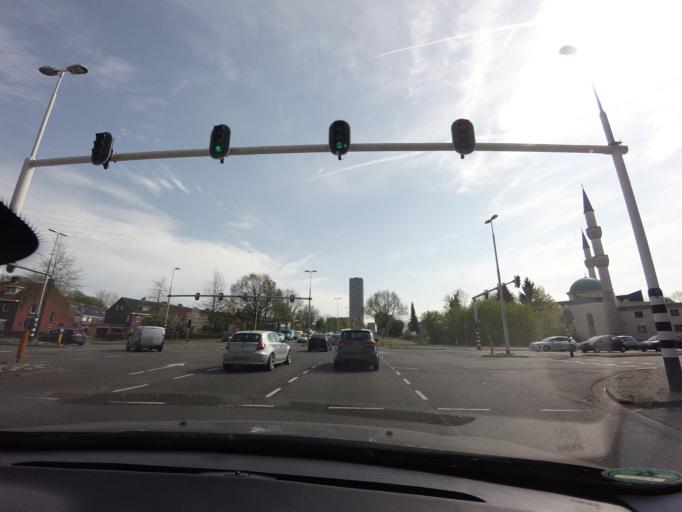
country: NL
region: North Brabant
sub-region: Gemeente Tilburg
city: Tilburg
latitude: 51.5666
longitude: 5.0656
